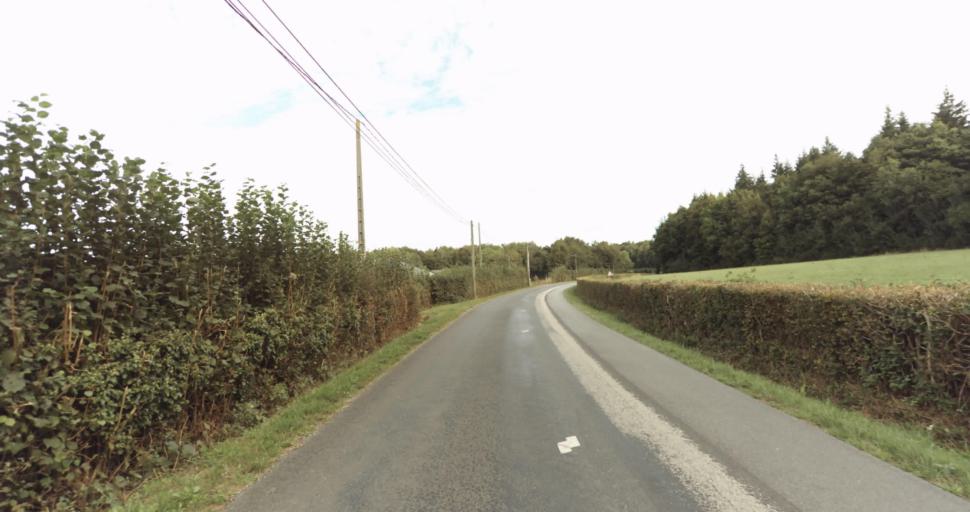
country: FR
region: Lower Normandy
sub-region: Departement de l'Orne
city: Gace
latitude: 48.8186
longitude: 0.2332
